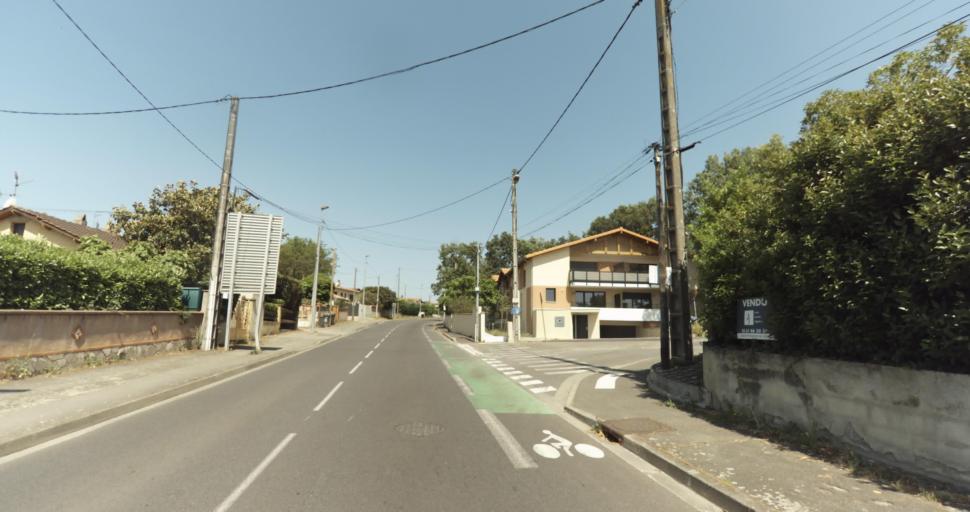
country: FR
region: Midi-Pyrenees
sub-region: Departement de la Haute-Garonne
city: Plaisance-du-Touch
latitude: 43.5690
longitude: 1.2883
